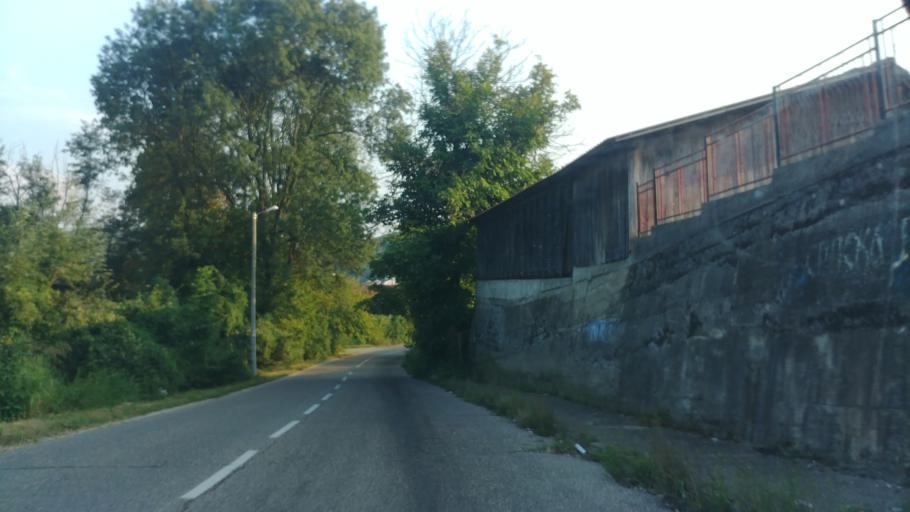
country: BA
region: Republika Srpska
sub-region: Opstina Ugljevik
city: Ugljevik
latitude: 44.7001
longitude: 18.9927
